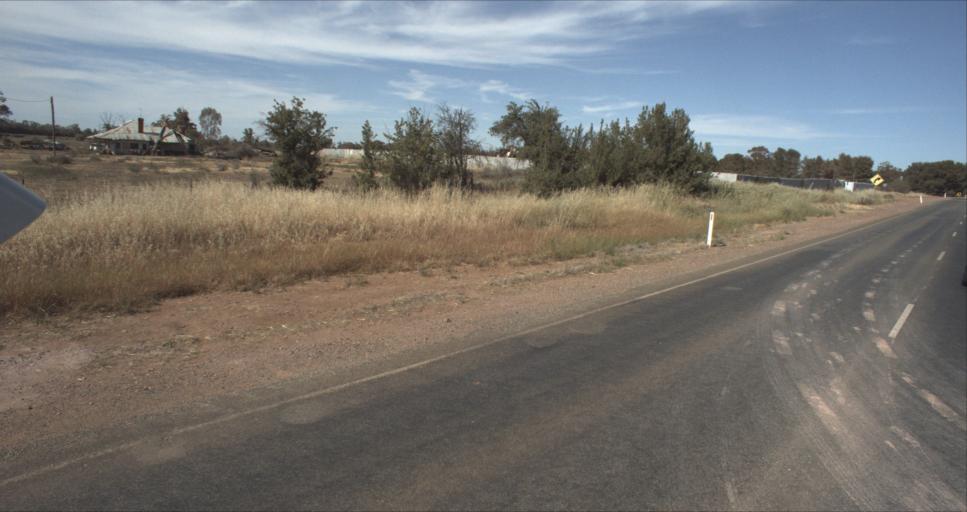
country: AU
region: New South Wales
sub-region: Leeton
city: Leeton
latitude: -34.5640
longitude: 146.4277
